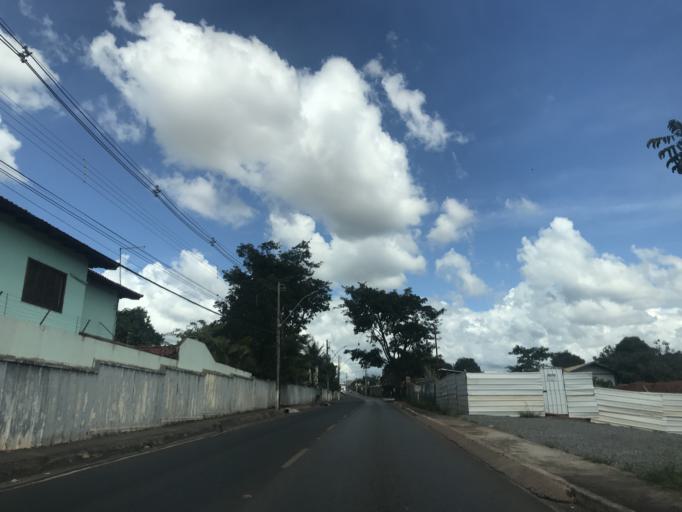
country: BR
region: Federal District
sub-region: Brasilia
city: Brasilia
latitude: -15.8733
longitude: -47.8017
